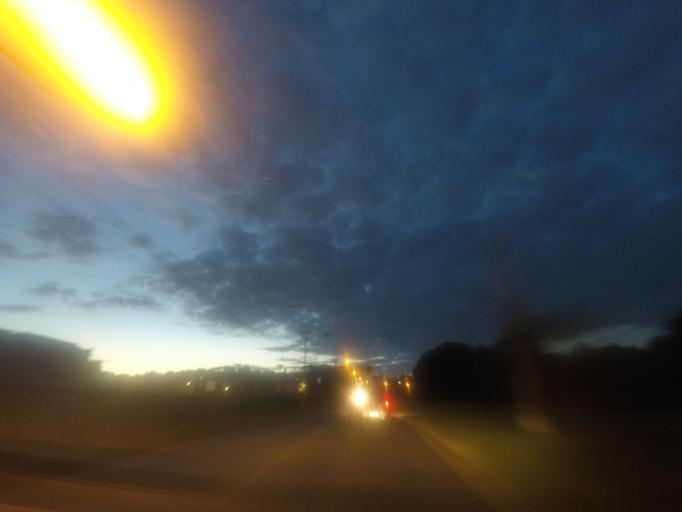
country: BR
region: Parana
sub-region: Pinhais
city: Pinhais
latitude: -25.3817
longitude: -49.2064
